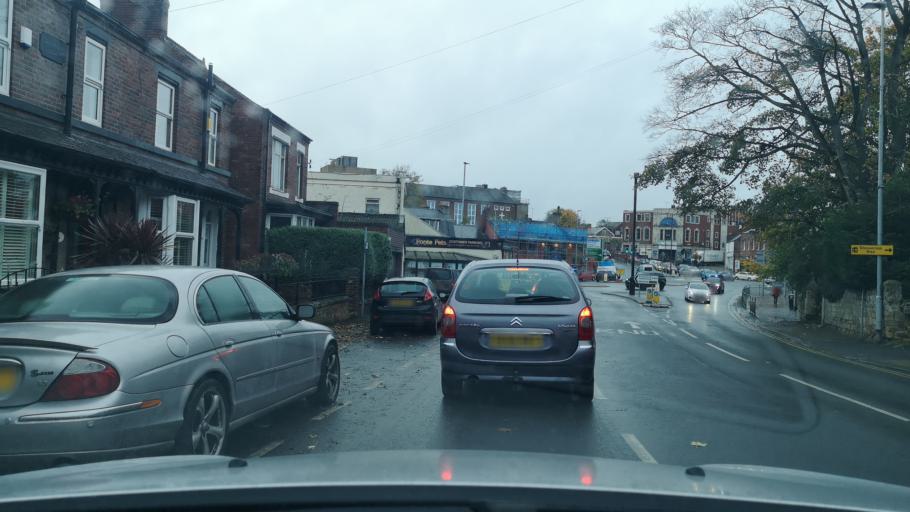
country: GB
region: England
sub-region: City and Borough of Wakefield
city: Pontefract
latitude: 53.6880
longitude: -1.3144
